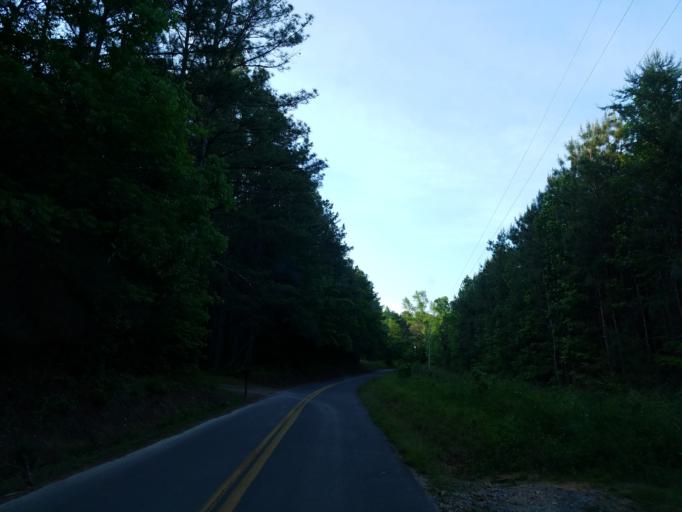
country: US
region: Georgia
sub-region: Gordon County
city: Calhoun
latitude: 34.5556
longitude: -85.1051
